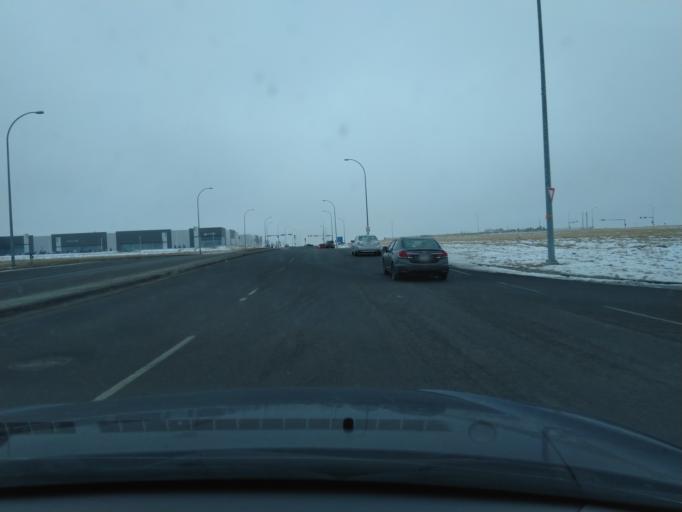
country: CA
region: Alberta
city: Airdrie
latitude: 51.1978
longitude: -113.9910
